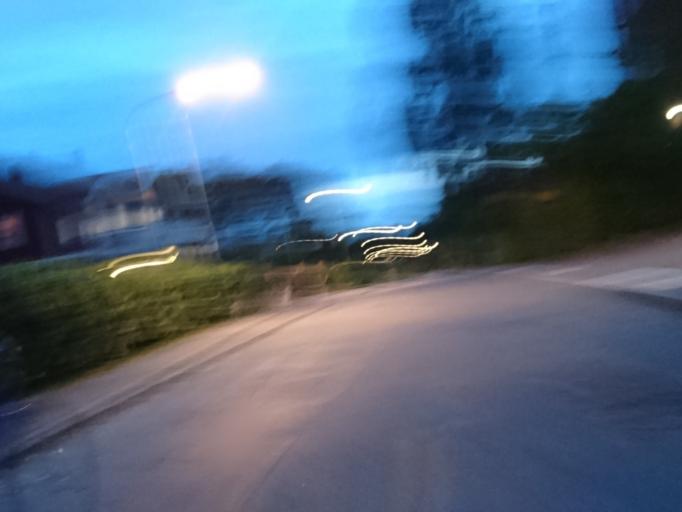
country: SE
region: Stockholm
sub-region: Huddinge Kommun
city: Huddinge
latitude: 59.2770
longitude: 17.9896
